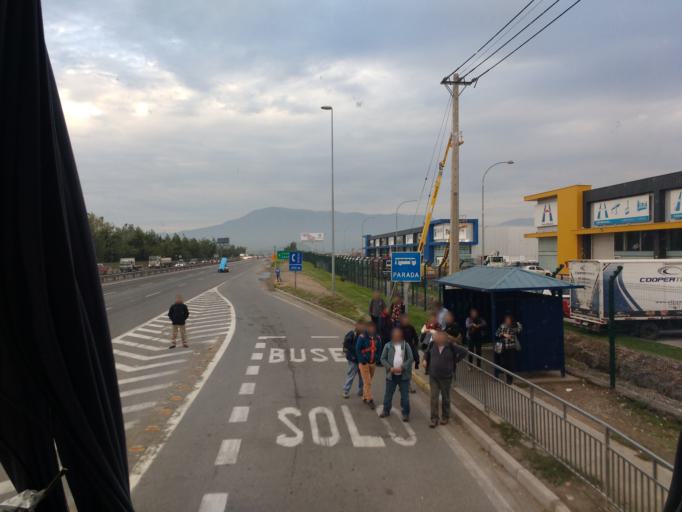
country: CL
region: Santiago Metropolitan
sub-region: Provincia de Santiago
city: Lo Prado
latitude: -33.4448
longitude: -70.7836
